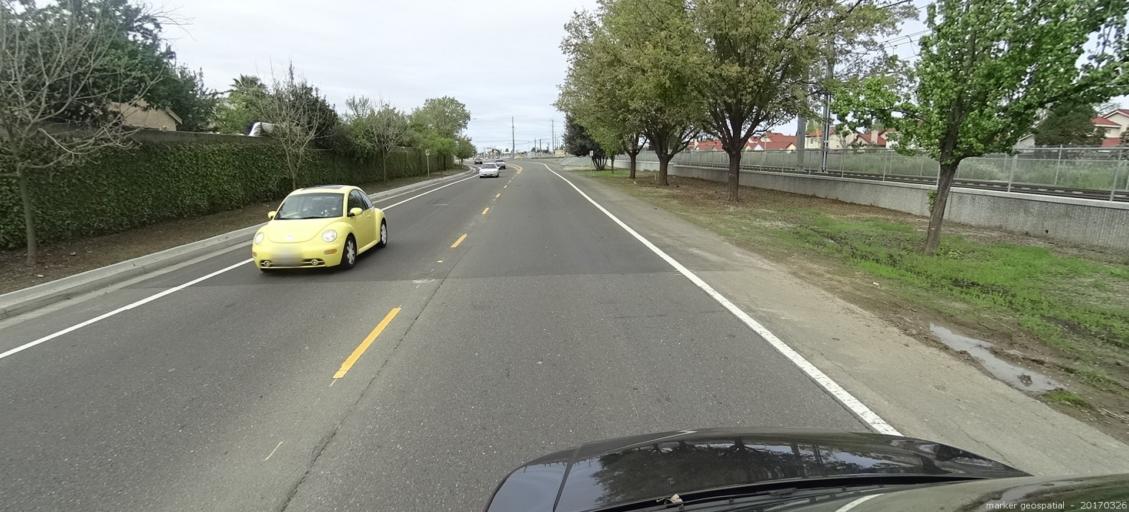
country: US
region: California
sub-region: Sacramento County
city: Parkway
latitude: 38.4619
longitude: -121.4430
